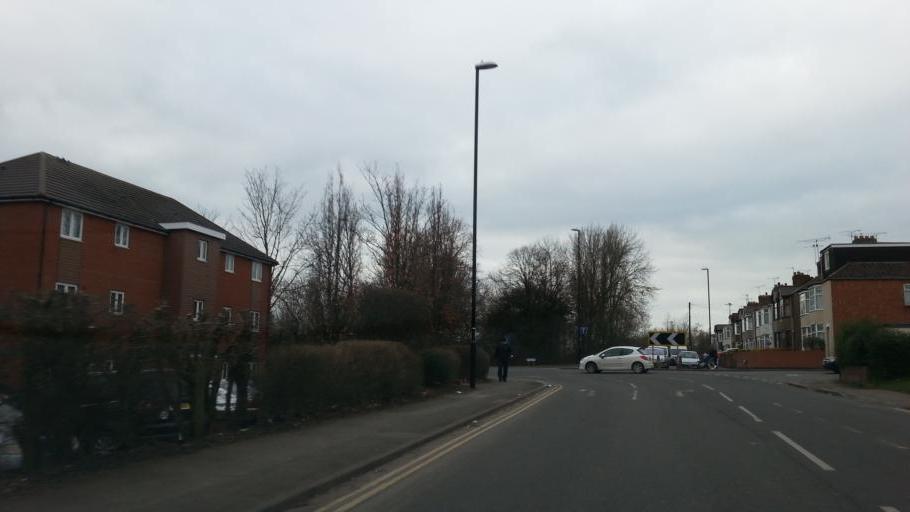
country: GB
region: England
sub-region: Coventry
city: Coventry
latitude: 52.4198
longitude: -1.4882
